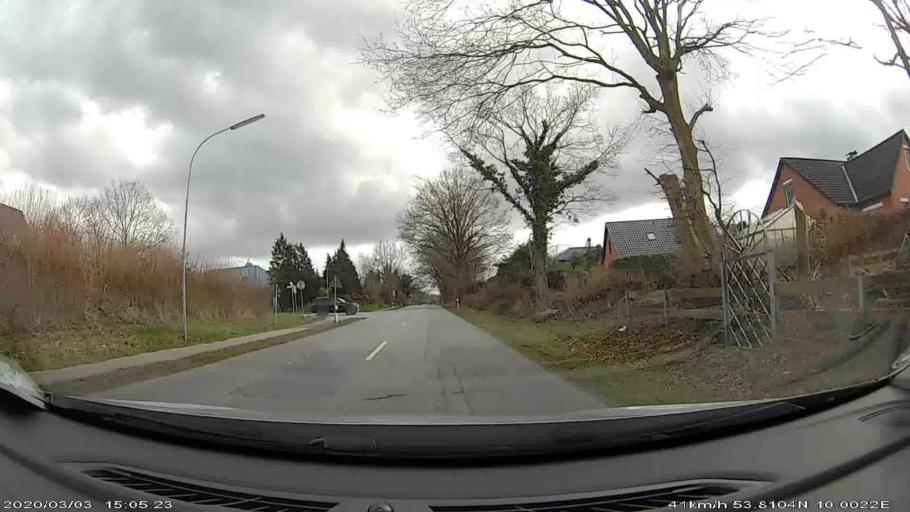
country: DE
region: Schleswig-Holstein
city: Kisdorf
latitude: 53.8106
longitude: 10.0021
